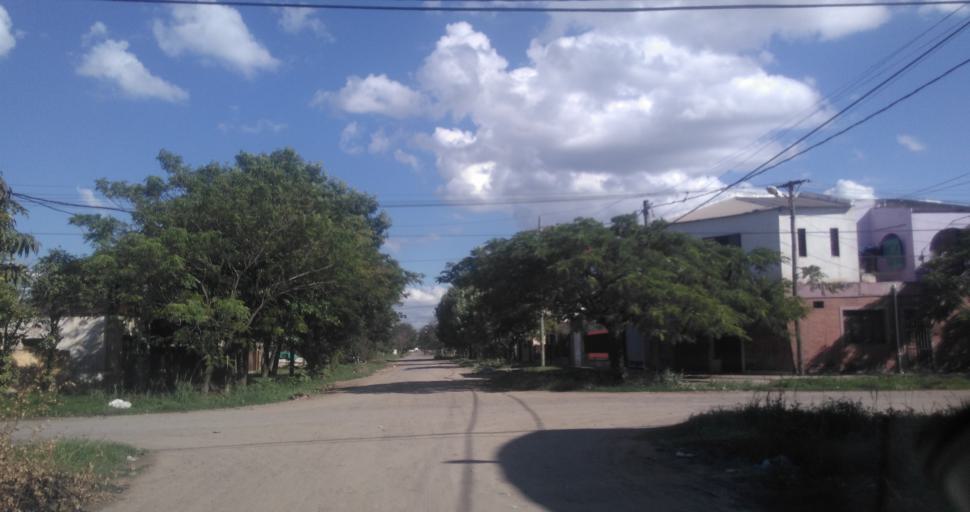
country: AR
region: Chaco
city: Resistencia
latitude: -27.4709
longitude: -58.9695
